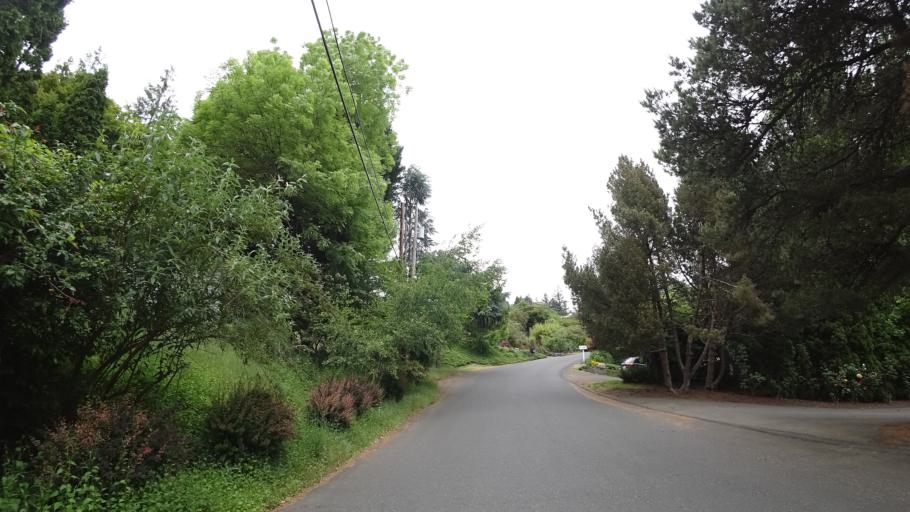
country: US
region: Oregon
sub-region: Multnomah County
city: Portland
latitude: 45.4830
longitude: -122.6934
